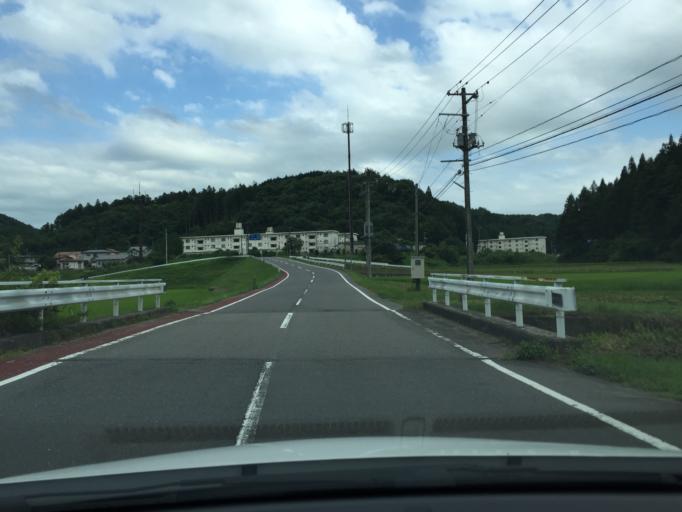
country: JP
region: Fukushima
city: Sukagawa
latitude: 37.1835
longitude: 140.2147
